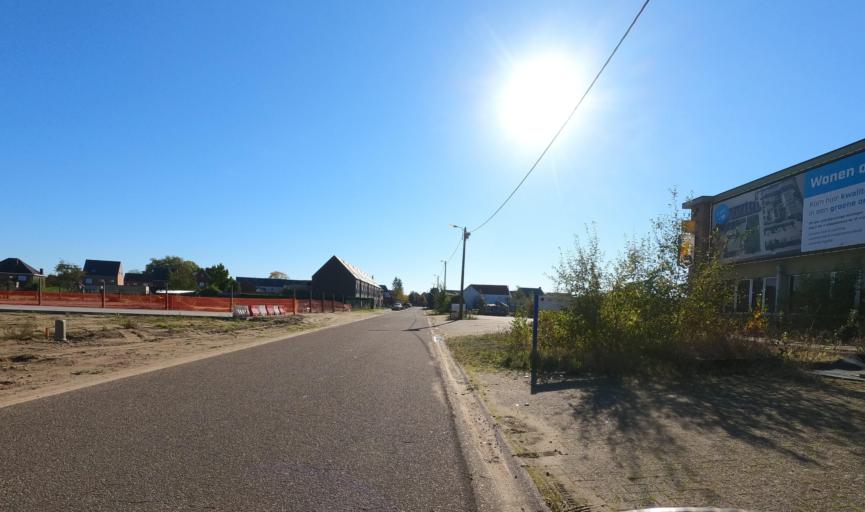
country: BE
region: Flanders
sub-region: Provincie Antwerpen
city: Hulshout
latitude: 51.1057
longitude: 4.7861
